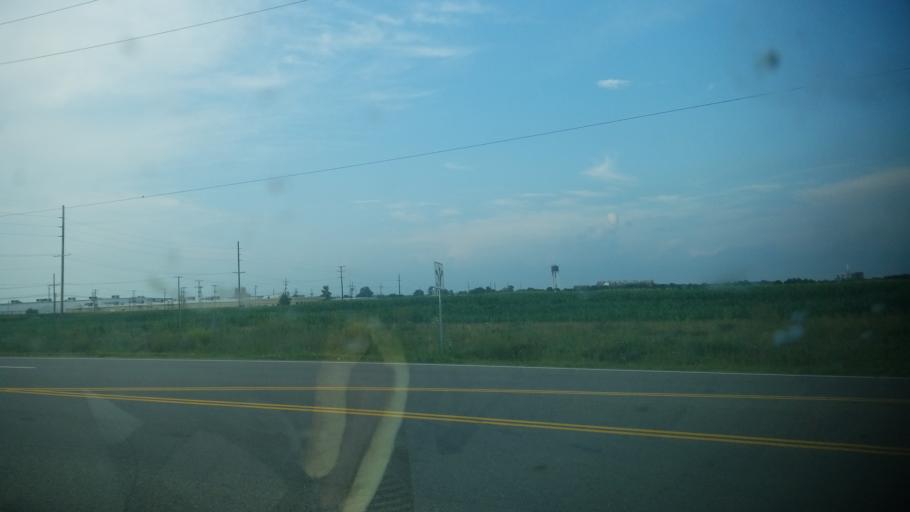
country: US
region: Ohio
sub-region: Pickaway County
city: Logan Elm Village
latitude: 39.5562
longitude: -82.9564
